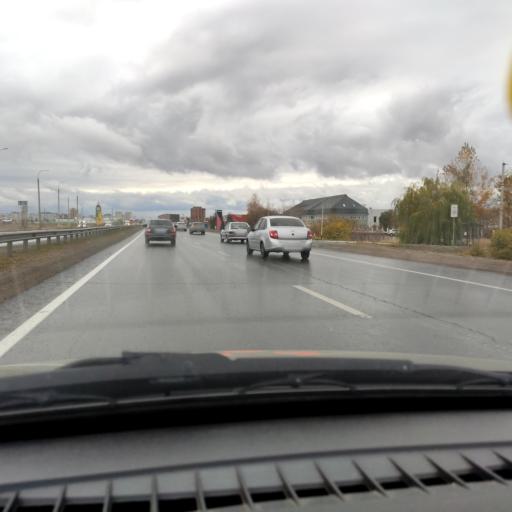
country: RU
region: Samara
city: Tol'yatti
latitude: 53.5599
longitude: 49.3566
